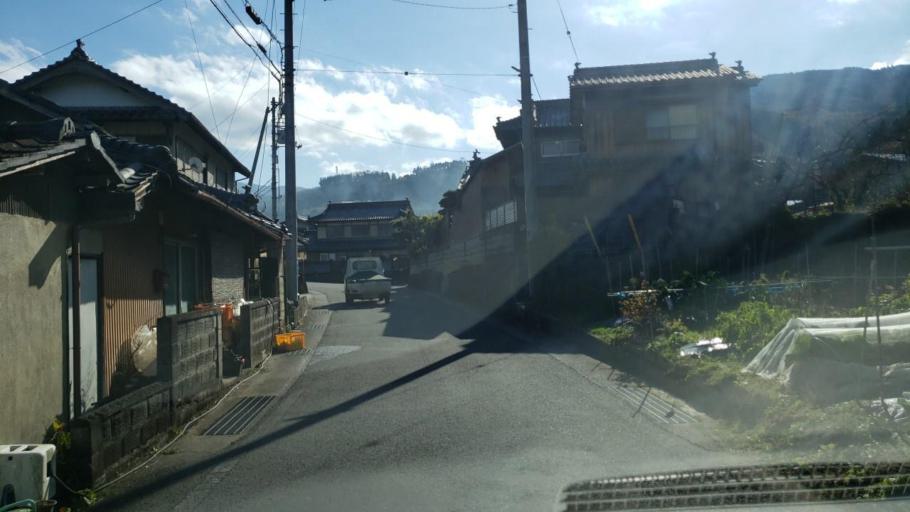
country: JP
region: Tokushima
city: Wakimachi
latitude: 34.0296
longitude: 134.0296
